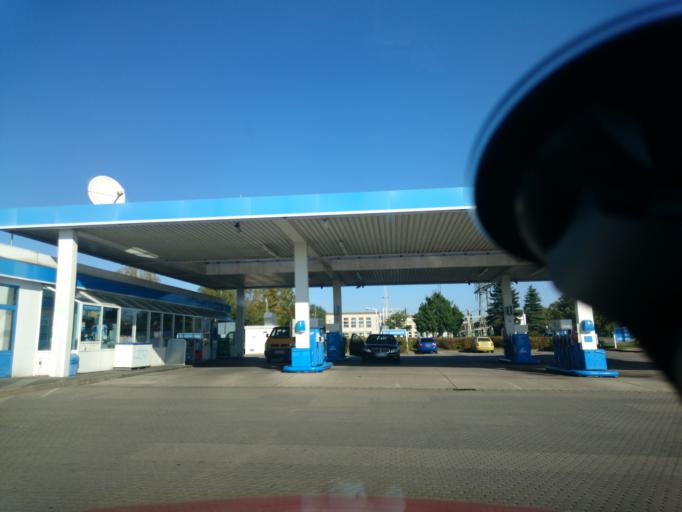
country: DE
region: Mecklenburg-Vorpommern
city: Ribnitz-Damgarten
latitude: 54.2393
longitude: 12.4070
